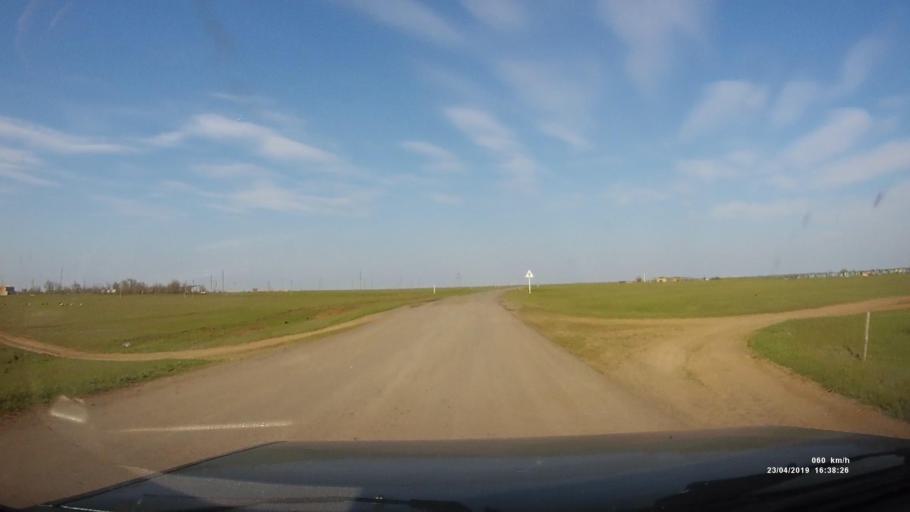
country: RU
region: Kalmykiya
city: Priyutnoye
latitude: 46.3355
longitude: 43.1534
